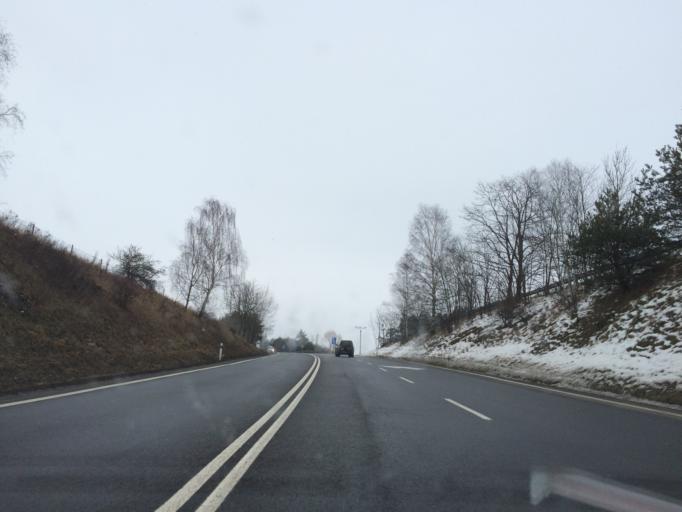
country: CZ
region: Jihocesky
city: Radomysl
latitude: 49.2938
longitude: 13.9870
